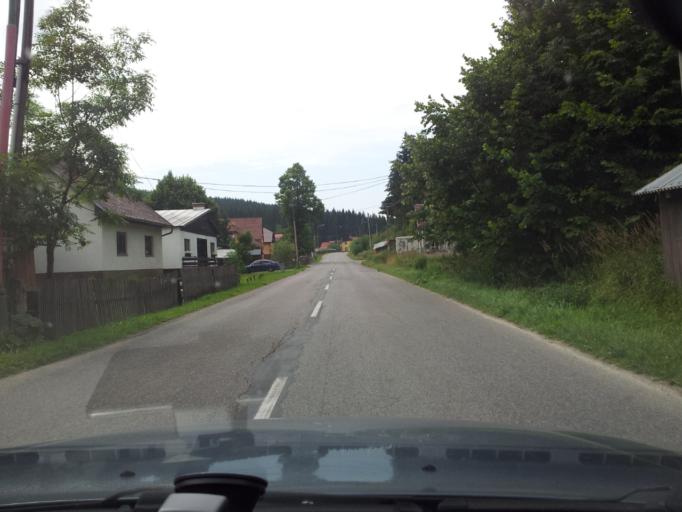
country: SK
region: Zilinsky
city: Oravska Lesna
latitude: 49.3710
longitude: 19.2156
